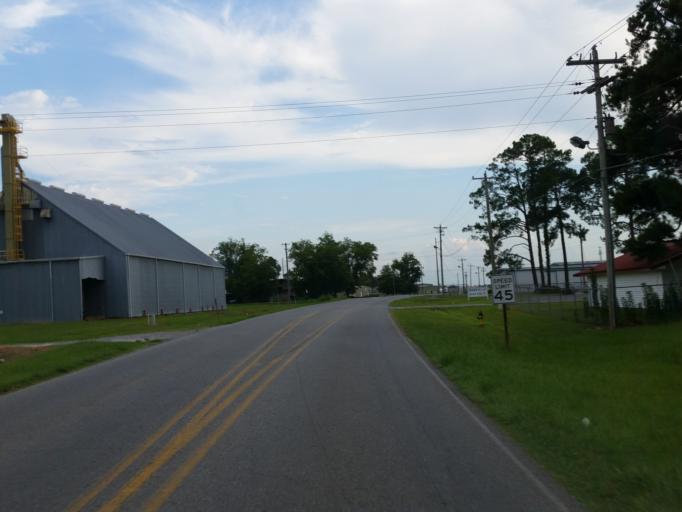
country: US
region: Georgia
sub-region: Cook County
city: Adel
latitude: 31.1194
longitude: -83.4200
